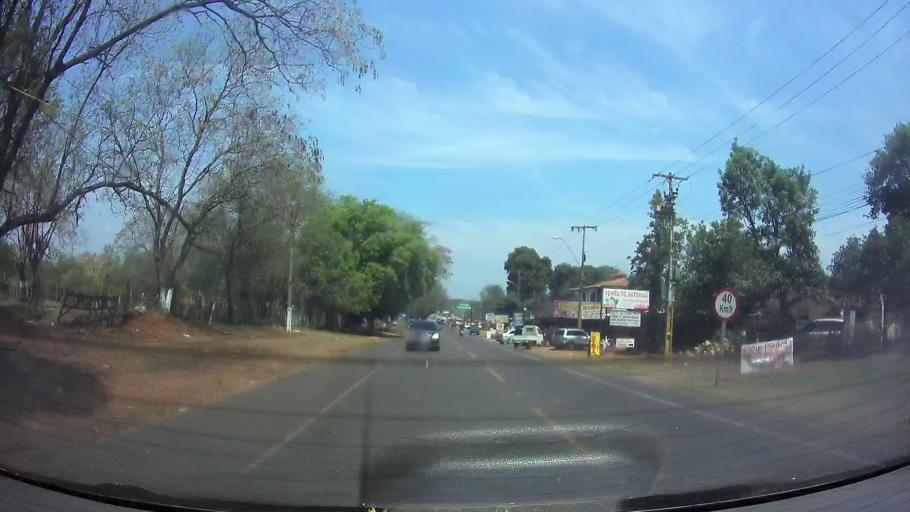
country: PY
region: Central
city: Capiata
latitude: -25.4131
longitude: -57.4583
